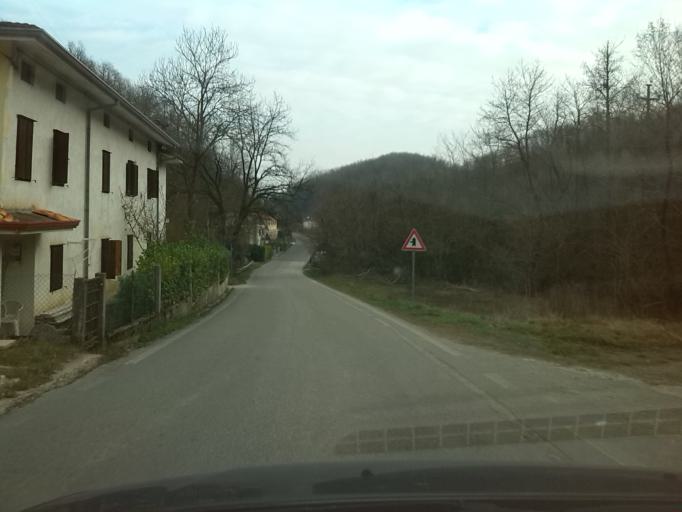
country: IT
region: Friuli Venezia Giulia
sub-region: Provincia di Gorizia
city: San Floriano del Collio
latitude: 45.9597
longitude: 13.5959
